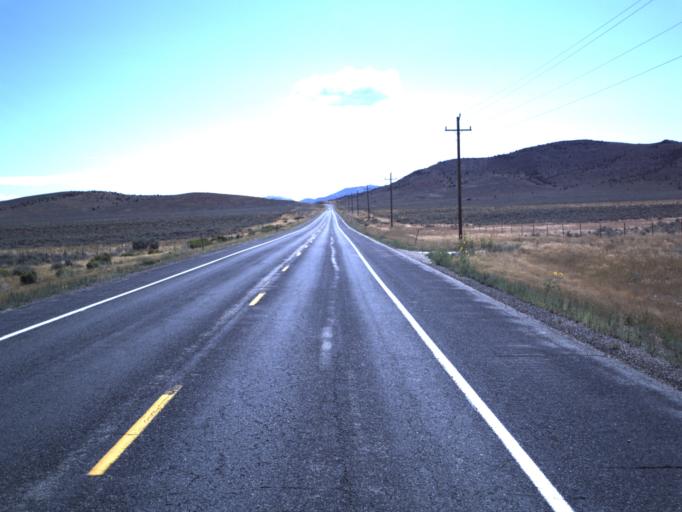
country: US
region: Utah
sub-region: Utah County
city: Eagle Mountain
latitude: 40.0774
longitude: -112.3930
